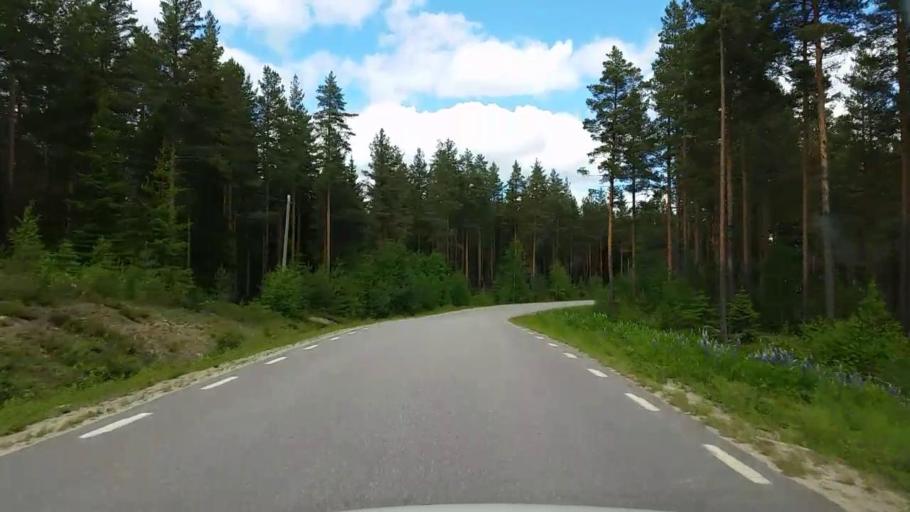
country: SE
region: Gaevleborg
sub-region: Ovanakers Kommun
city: Alfta
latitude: 61.4087
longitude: 16.0617
